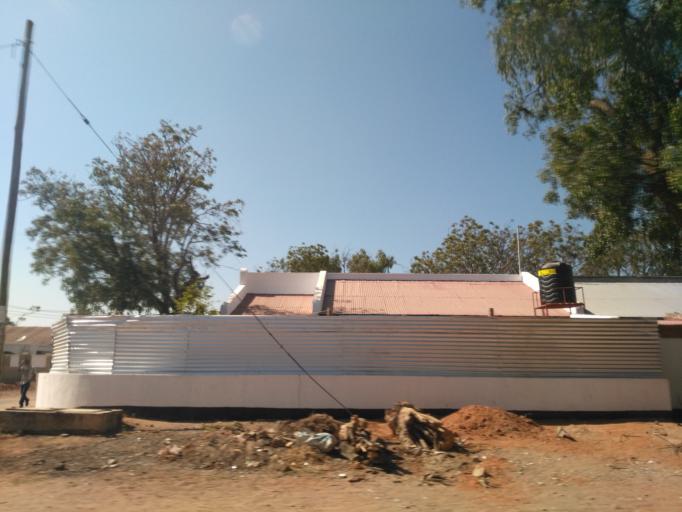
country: TZ
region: Dodoma
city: Dodoma
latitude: -6.1607
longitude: 35.7506
